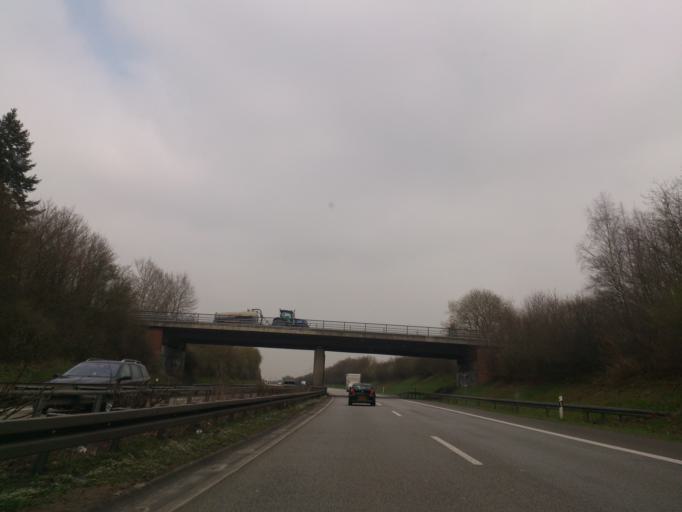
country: DE
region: North Rhine-Westphalia
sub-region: Regierungsbezirk Dusseldorf
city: Schwalmtal
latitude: 51.2011
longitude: 6.3000
